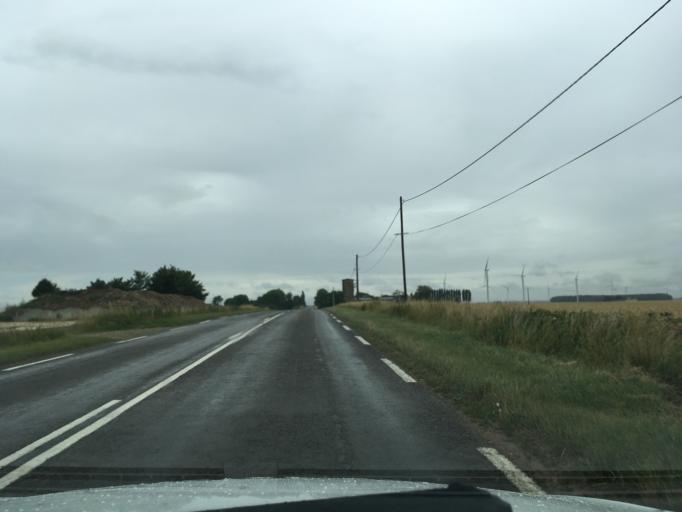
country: FR
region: Picardie
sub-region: Departement de l'Aisne
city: Esqueheries
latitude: 49.9354
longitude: 3.7285
